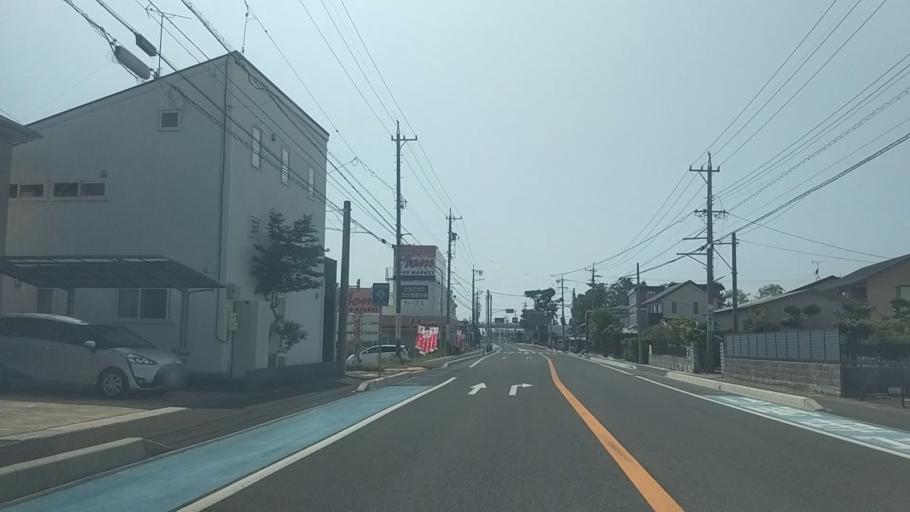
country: JP
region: Shizuoka
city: Hamamatsu
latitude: 34.6884
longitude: 137.6937
